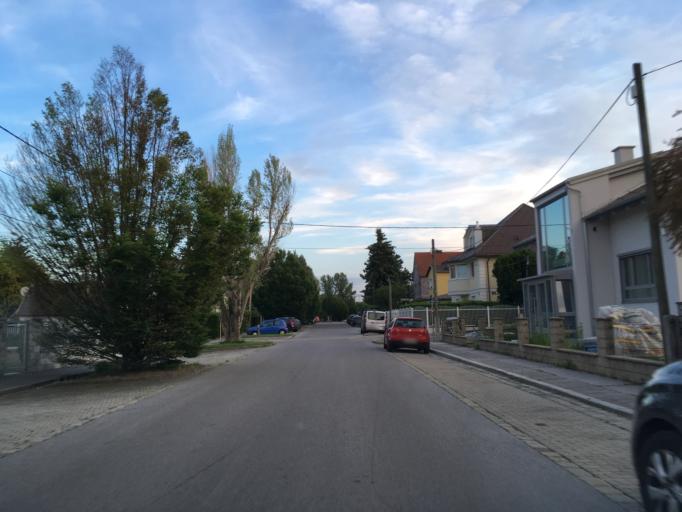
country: AT
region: Vienna
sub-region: Wien Stadt
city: Vienna
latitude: 48.2434
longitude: 16.4042
